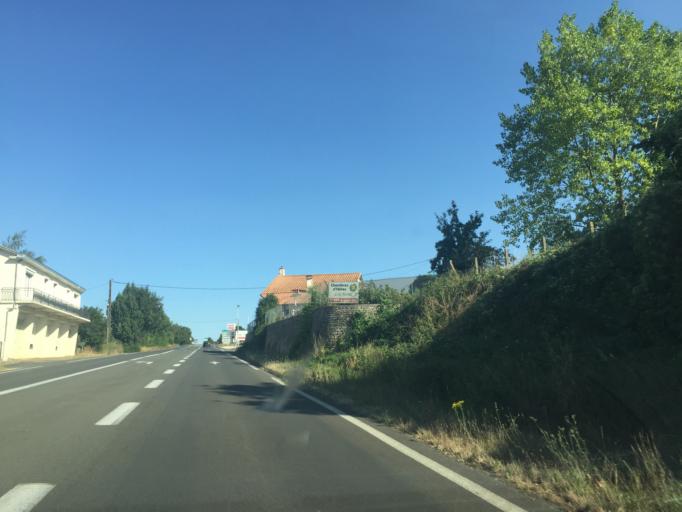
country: FR
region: Poitou-Charentes
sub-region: Departement des Deux-Sevres
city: Melle
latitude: 46.2055
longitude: -0.0982
